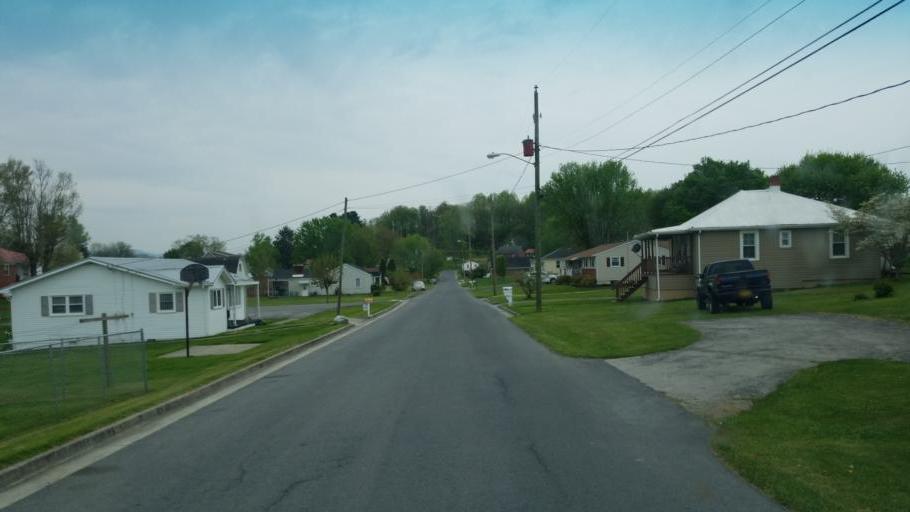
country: US
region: Virginia
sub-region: Smyth County
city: Marion
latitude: 36.8441
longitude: -81.5238
